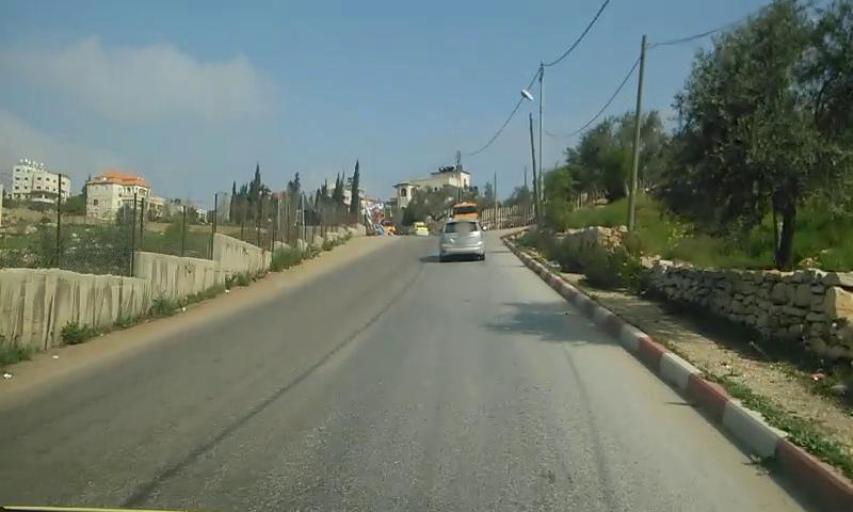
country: PS
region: West Bank
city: `Ayn Yabrud
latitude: 31.9533
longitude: 35.2473
